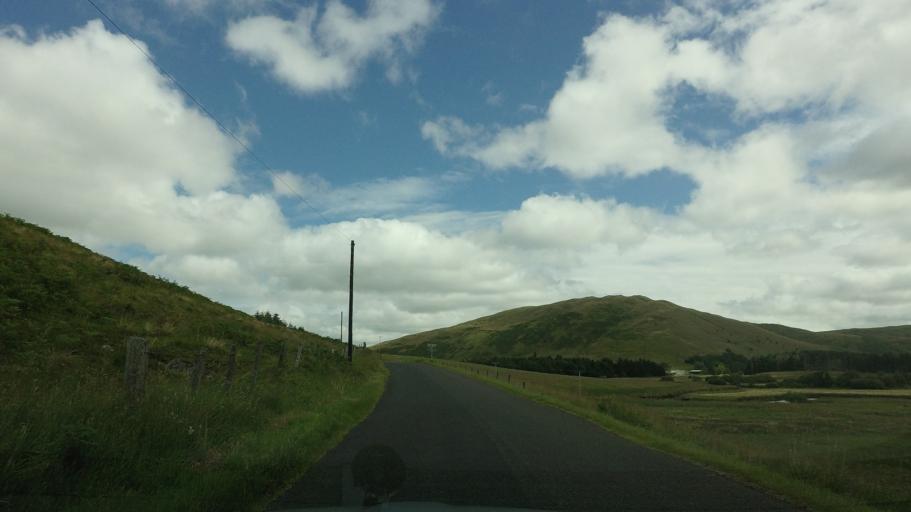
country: GB
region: Scotland
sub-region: The Scottish Borders
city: Innerleithen
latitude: 55.4400
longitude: -3.1085
